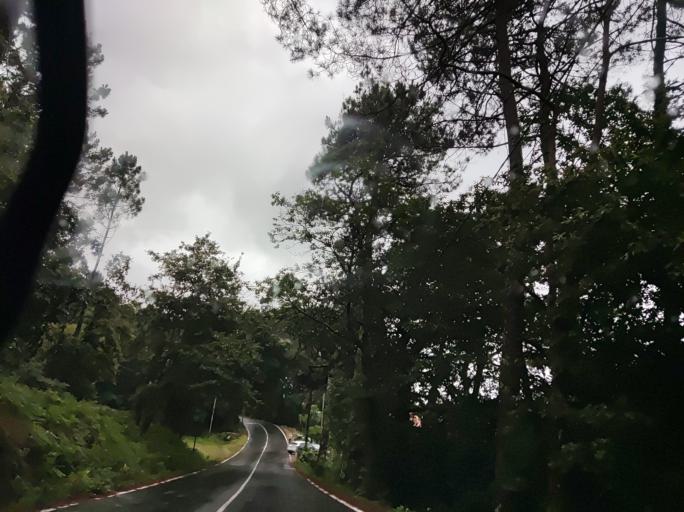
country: ES
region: Galicia
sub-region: Provincia da Coruna
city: Rianxo
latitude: 42.6945
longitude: -8.8422
